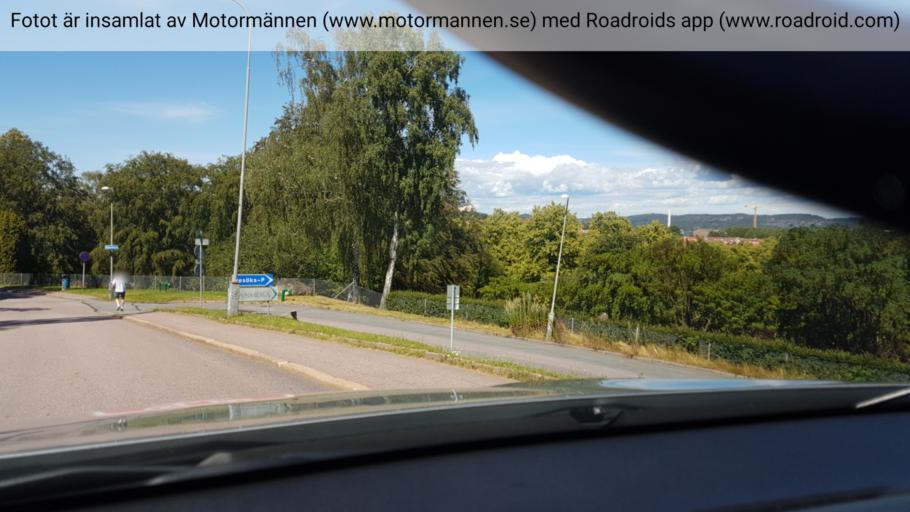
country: SE
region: Vaestra Goetaland
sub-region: Goteborg
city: Goeteborg
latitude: 57.7125
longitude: 12.0149
